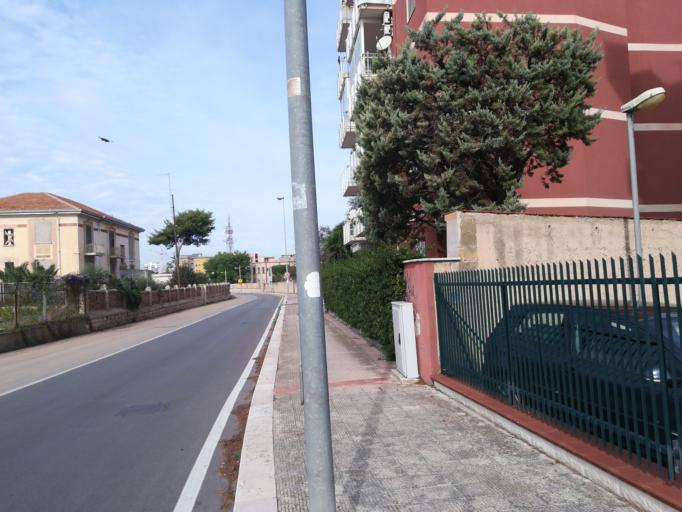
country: IT
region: Apulia
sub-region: Provincia di Bari
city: Bari
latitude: 41.1114
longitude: 16.8892
